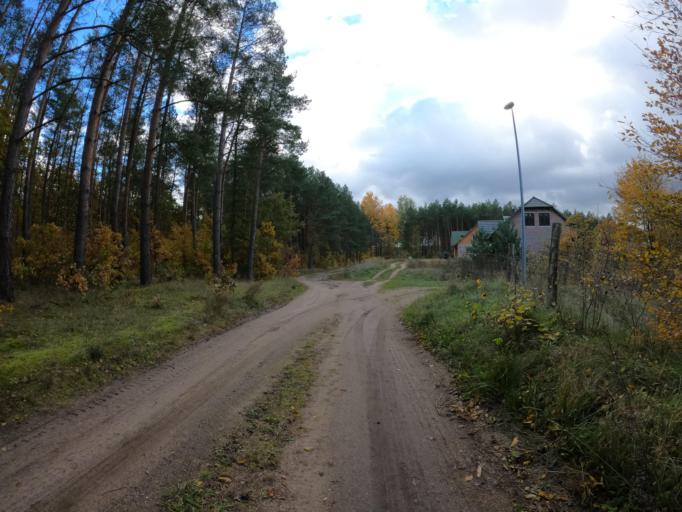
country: PL
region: West Pomeranian Voivodeship
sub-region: Powiat mysliborski
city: Barlinek
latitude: 52.9201
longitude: 15.2911
